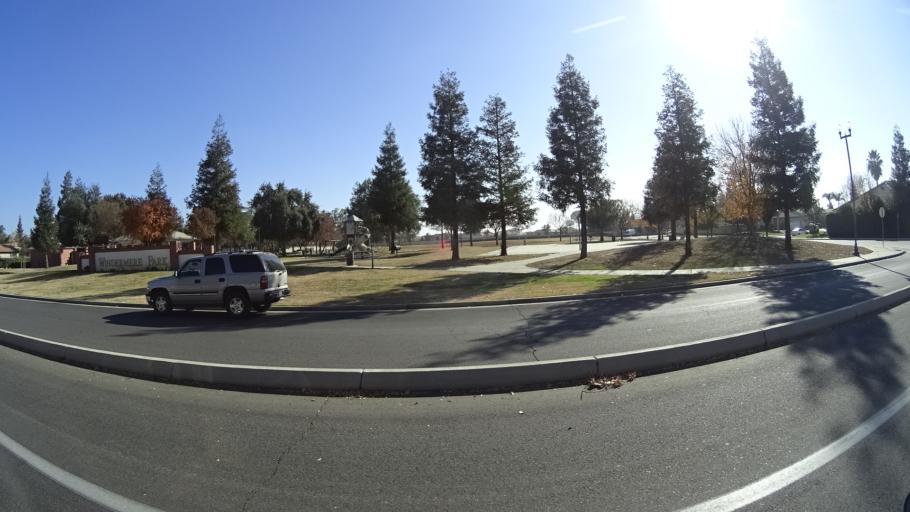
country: US
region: California
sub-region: Kern County
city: Rosedale
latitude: 35.3278
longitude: -119.1341
